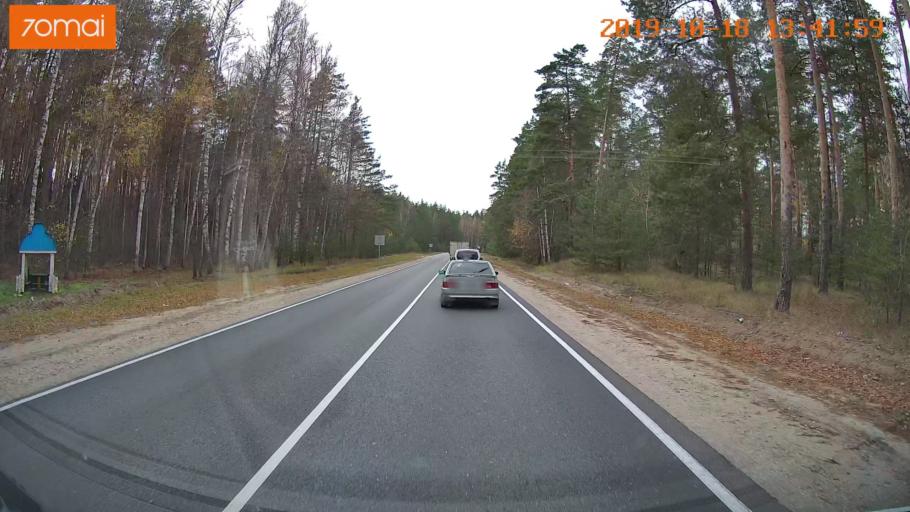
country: RU
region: Rjazan
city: Solotcha
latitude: 54.9245
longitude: 39.9948
